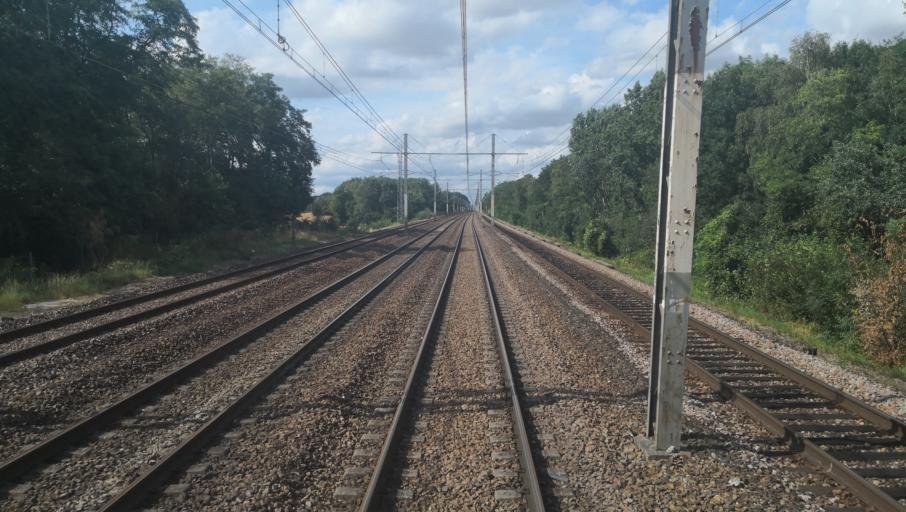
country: FR
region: Ile-de-France
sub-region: Departement de l'Essonne
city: Cheptainville
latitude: 48.5430
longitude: 2.2931
